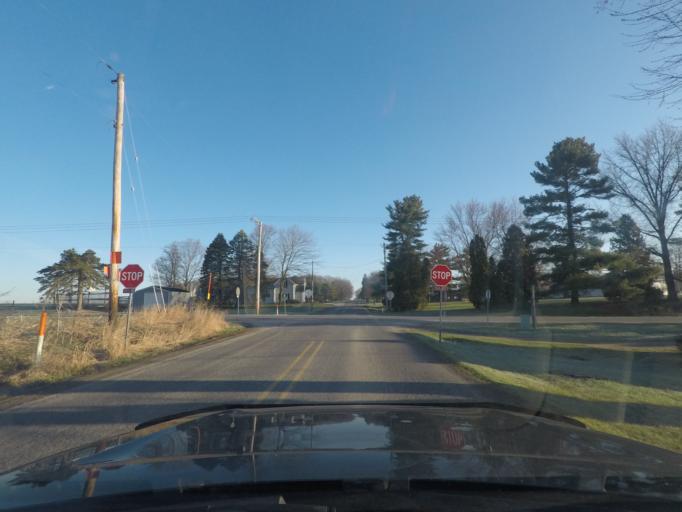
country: US
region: Indiana
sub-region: Elkhart County
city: Dunlap
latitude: 41.5944
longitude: -85.9254
